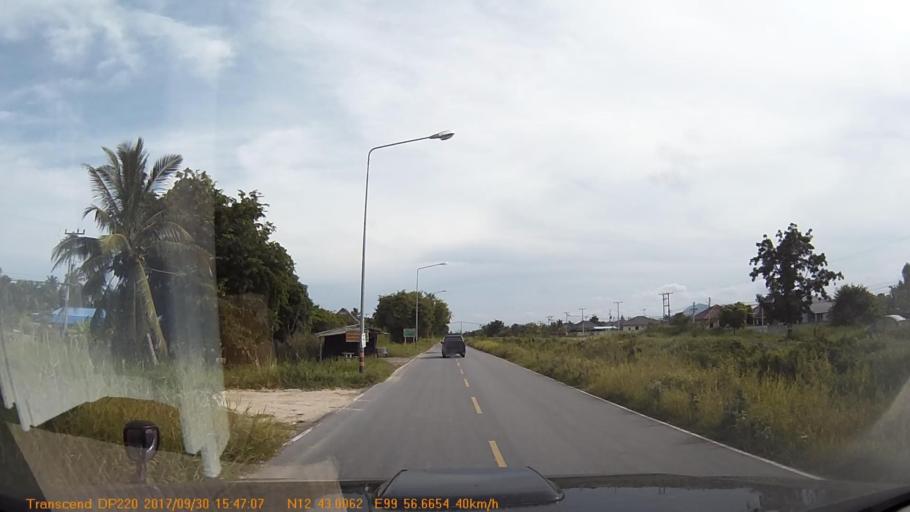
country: TH
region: Phetchaburi
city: Cha-am
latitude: 12.7164
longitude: 99.9444
